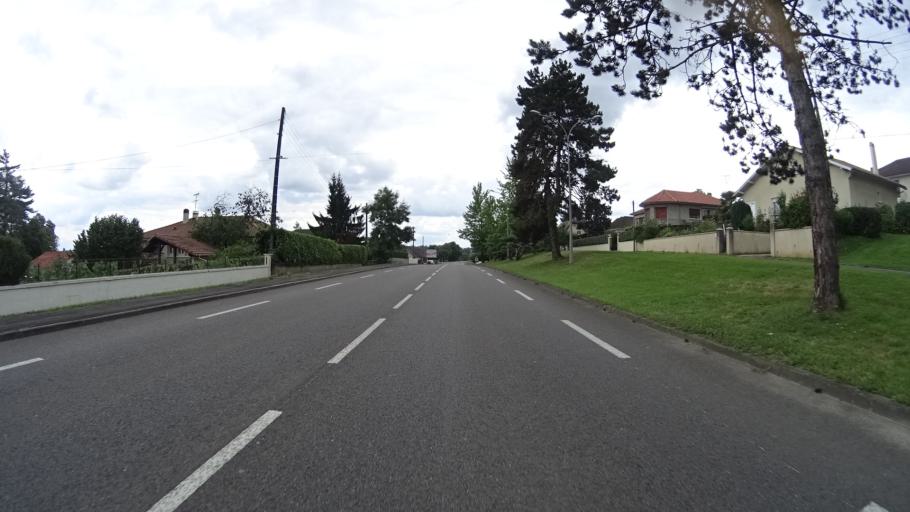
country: FR
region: Aquitaine
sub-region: Departement des Pyrenees-Atlantiques
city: Orthez
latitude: 43.4945
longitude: -0.7798
